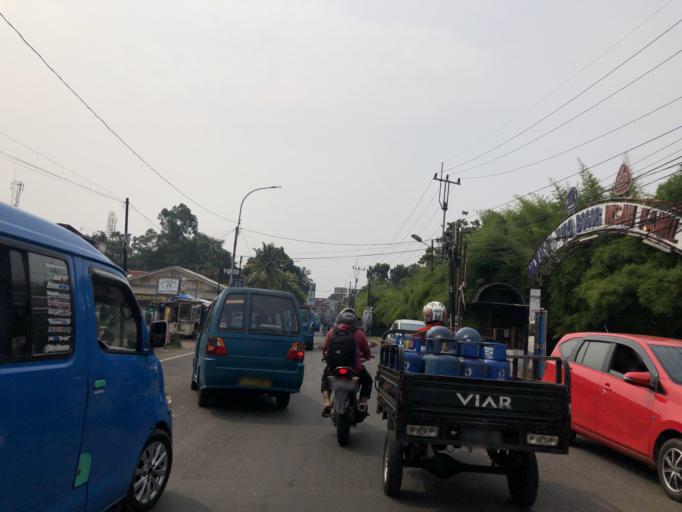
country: ID
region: West Java
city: Bogor
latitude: -6.5734
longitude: 106.7513
